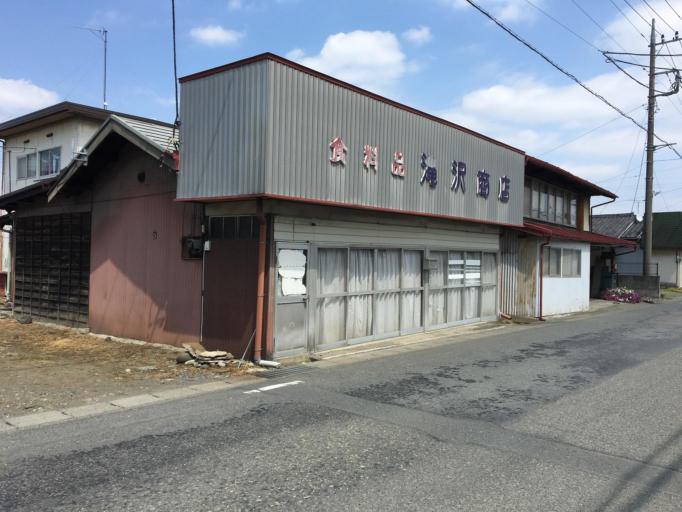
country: JP
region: Gunma
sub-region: Sawa-gun
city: Tamamura
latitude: 36.2871
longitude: 139.1604
